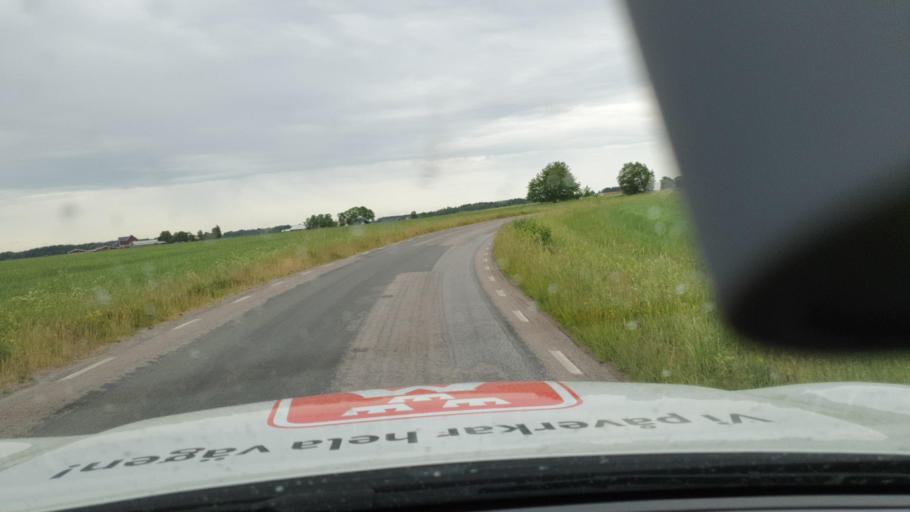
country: SE
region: Vaestra Goetaland
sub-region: Tidaholms Kommun
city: Olofstorp
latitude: 58.3369
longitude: 13.9879
